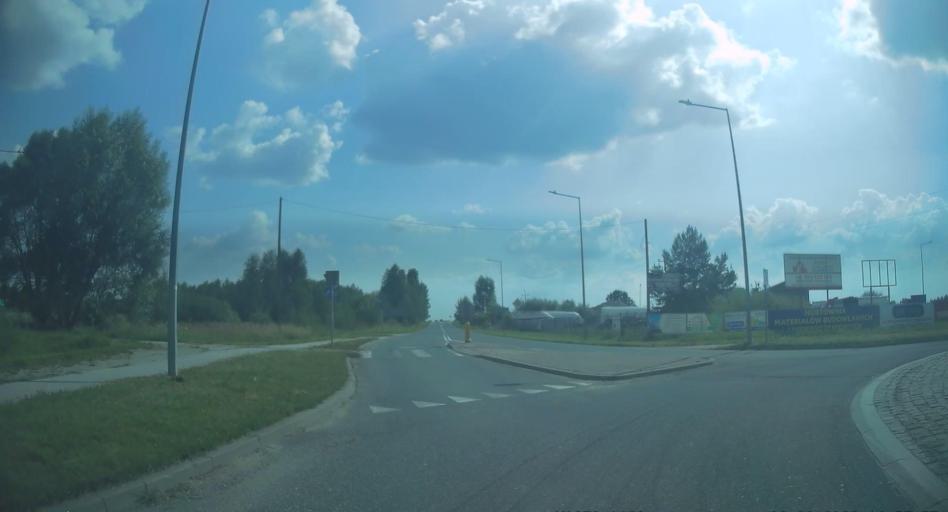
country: PL
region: Swietokrzyskie
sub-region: Powiat kielecki
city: Lopuszno
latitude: 50.9340
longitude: 20.2404
